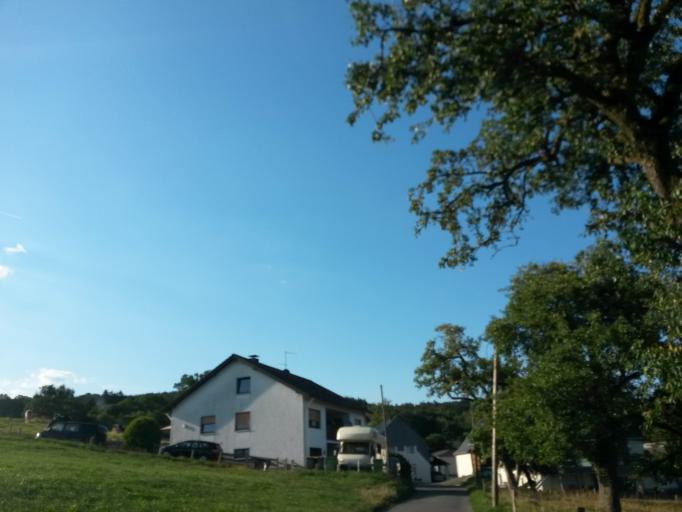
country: DE
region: North Rhine-Westphalia
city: Meinerzhagen
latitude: 51.1078
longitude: 7.6944
